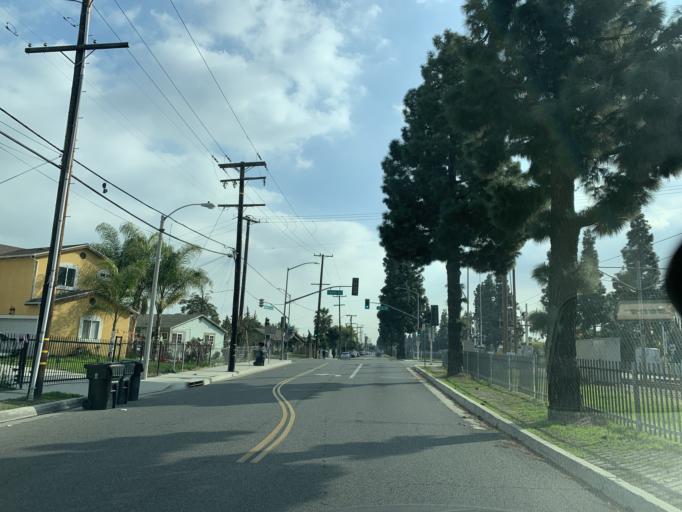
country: US
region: California
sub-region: Los Angeles County
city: Willowbrook
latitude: 33.9204
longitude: -118.2334
